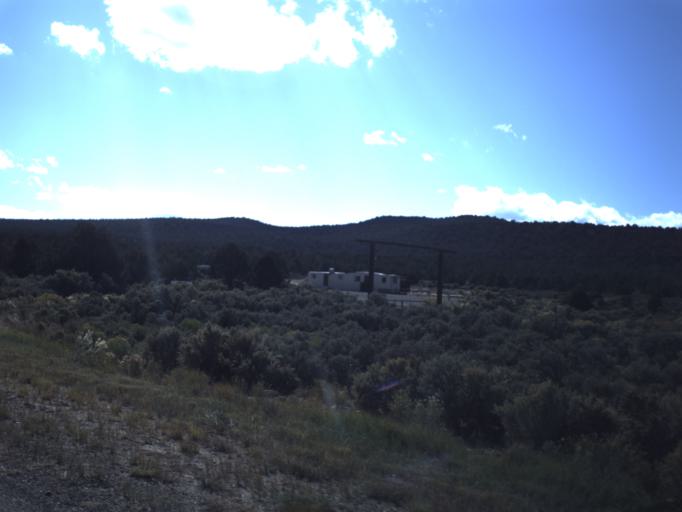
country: US
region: Utah
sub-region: Garfield County
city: Panguitch
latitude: 37.7896
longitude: -112.4392
